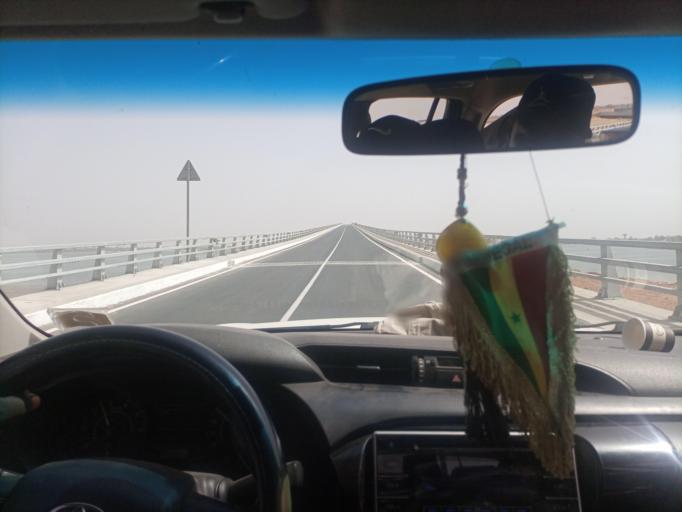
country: SN
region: Fatick
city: Foundiougne
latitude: 14.1422
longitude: -16.4716
